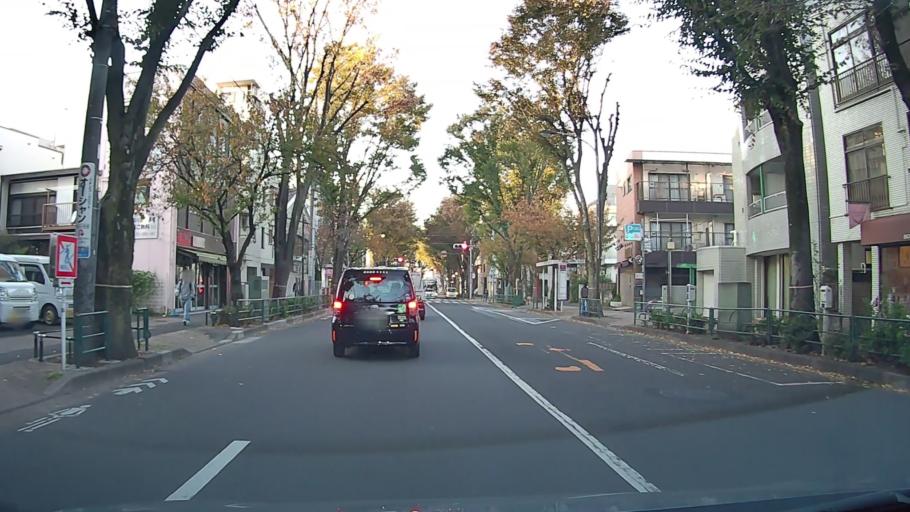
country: JP
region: Tokyo
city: Tokyo
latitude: 35.7121
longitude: 139.6350
